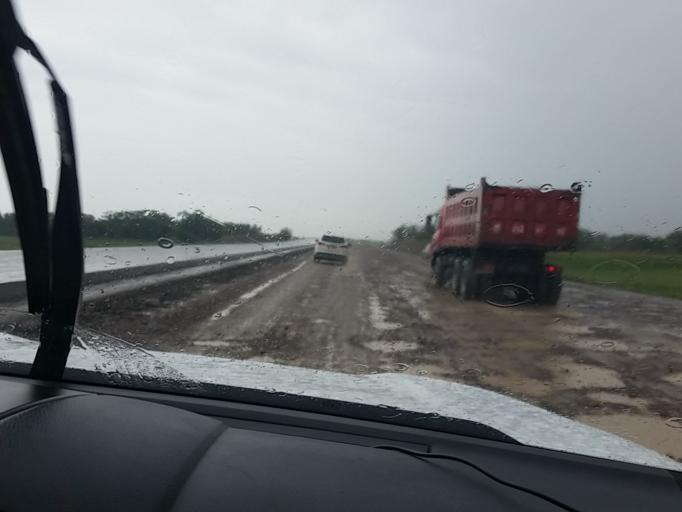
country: KZ
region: Almaty Oblysy
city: Turgen'
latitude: 43.5248
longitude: 77.5377
